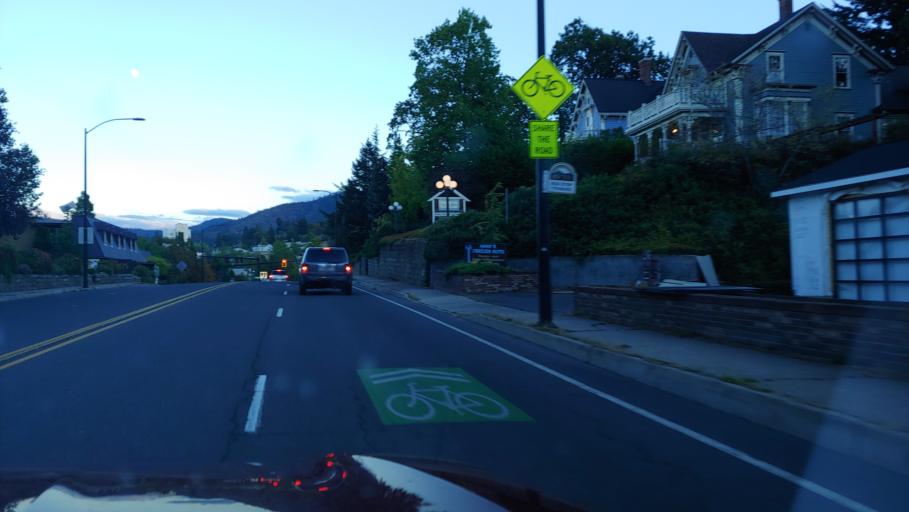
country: US
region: Oregon
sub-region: Jackson County
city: Ashland
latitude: 42.2000
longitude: -122.7174
